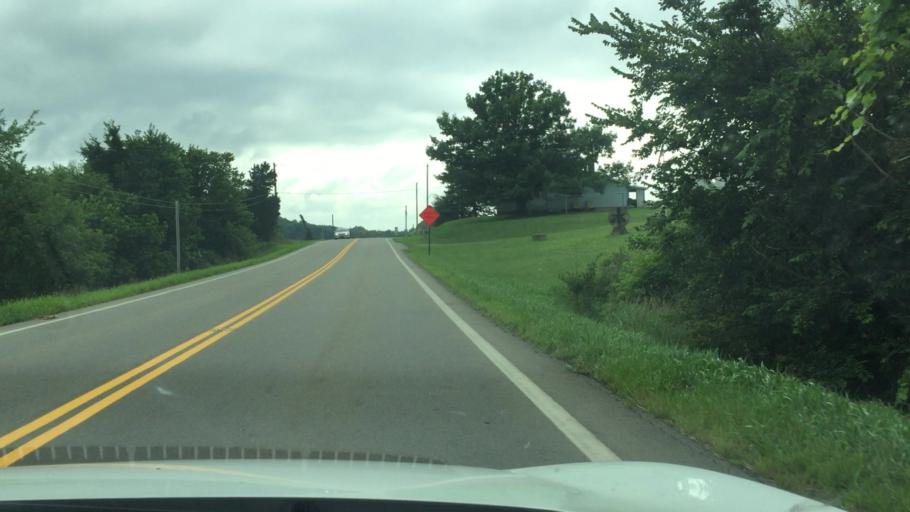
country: US
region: Ohio
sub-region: Champaign County
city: Mechanicsburg
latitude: 40.0533
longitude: -83.6060
